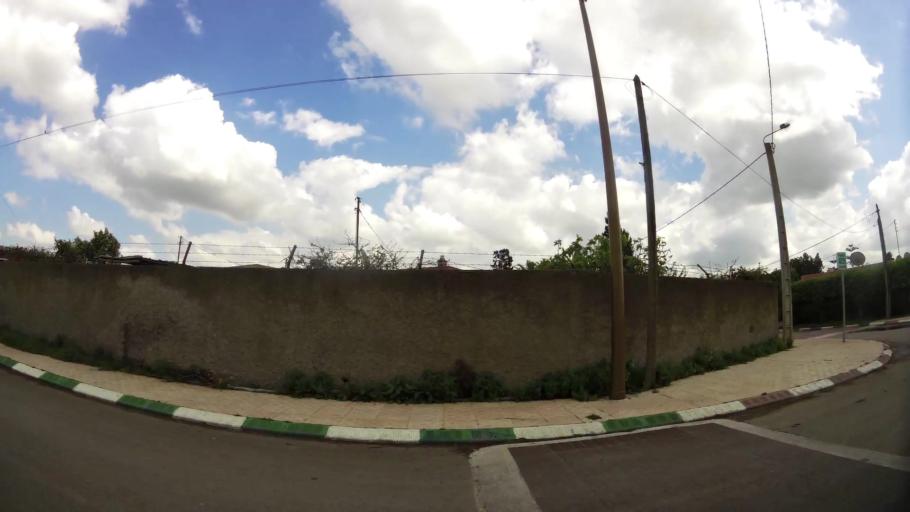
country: MA
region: Grand Casablanca
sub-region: Mediouna
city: Mediouna
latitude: 33.3840
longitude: -7.5410
